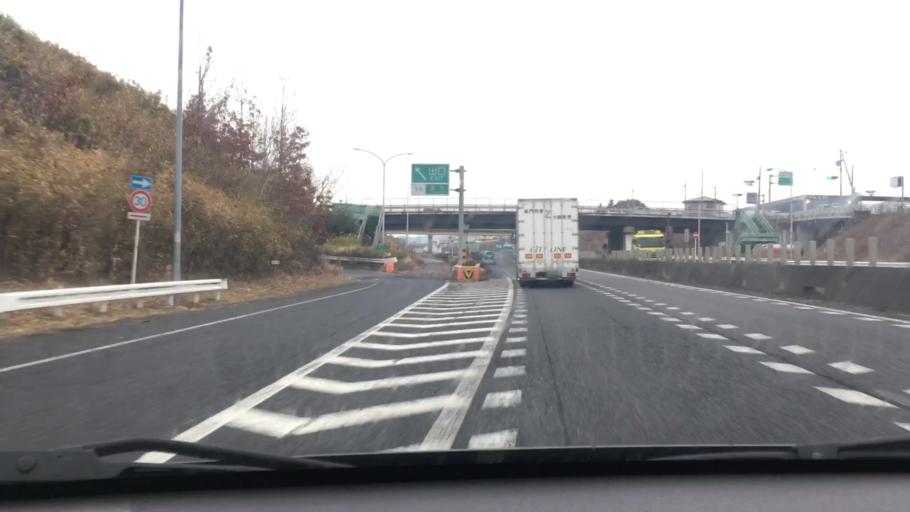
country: JP
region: Mie
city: Ueno-ebisumachi
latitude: 34.7541
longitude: 136.1457
